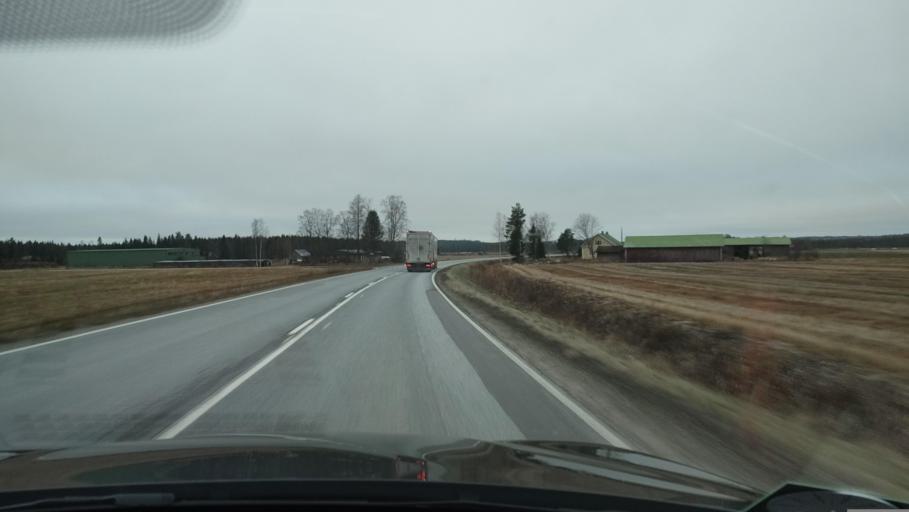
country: FI
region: Southern Ostrobothnia
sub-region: Suupohja
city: Kauhajoki
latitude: 62.3853
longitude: 22.1387
